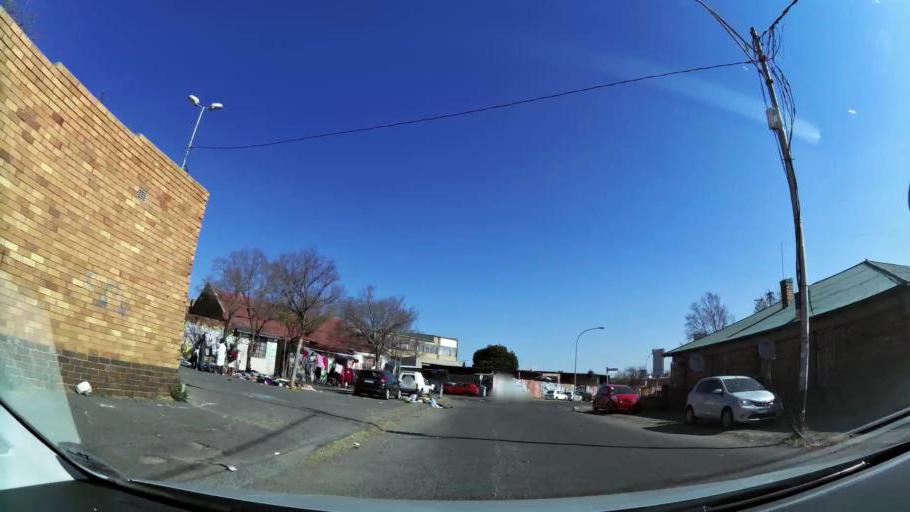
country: ZA
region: Gauteng
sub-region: City of Johannesburg Metropolitan Municipality
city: Johannesburg
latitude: -26.2017
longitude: 28.0658
